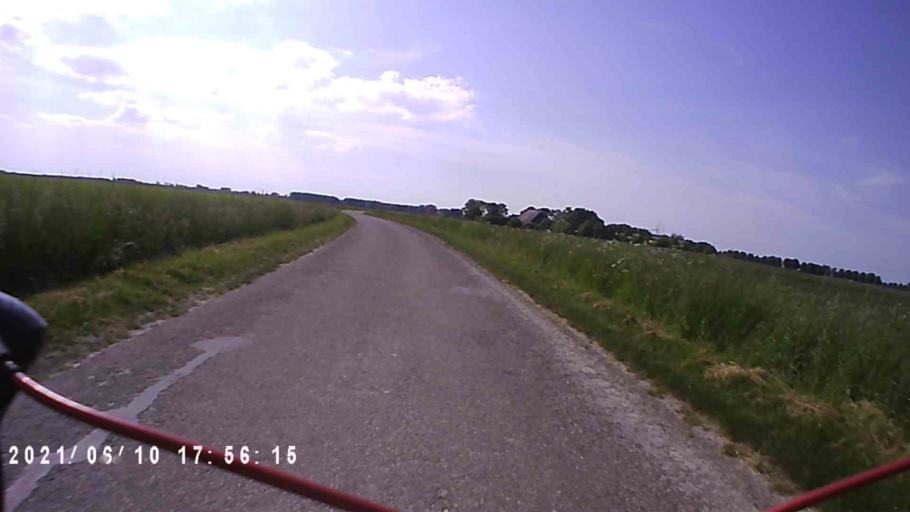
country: NL
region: Groningen
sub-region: Gemeente De Marne
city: Ulrum
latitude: 53.3304
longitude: 6.3319
